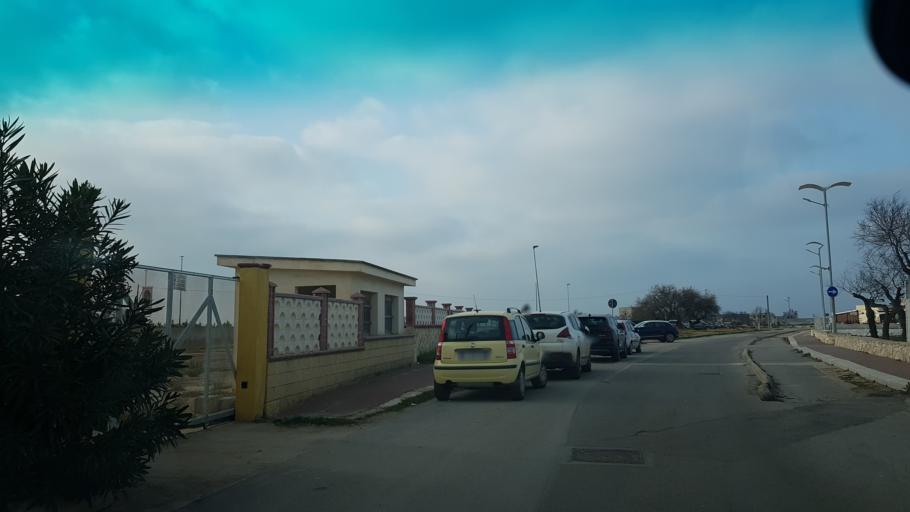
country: IT
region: Apulia
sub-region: Provincia di Brindisi
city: Carovigno
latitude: 40.7417
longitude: 17.7357
